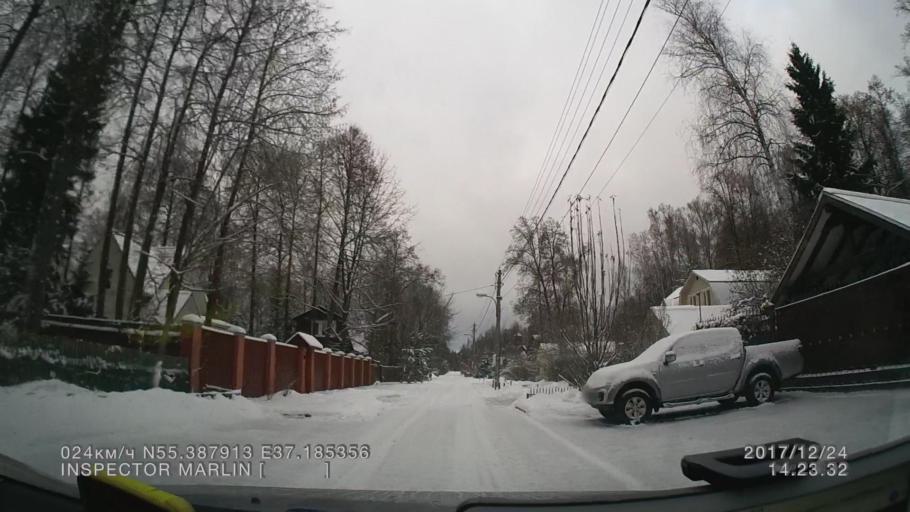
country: RU
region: Moskovskaya
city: Troitsk
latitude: 55.3880
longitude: 37.1852
